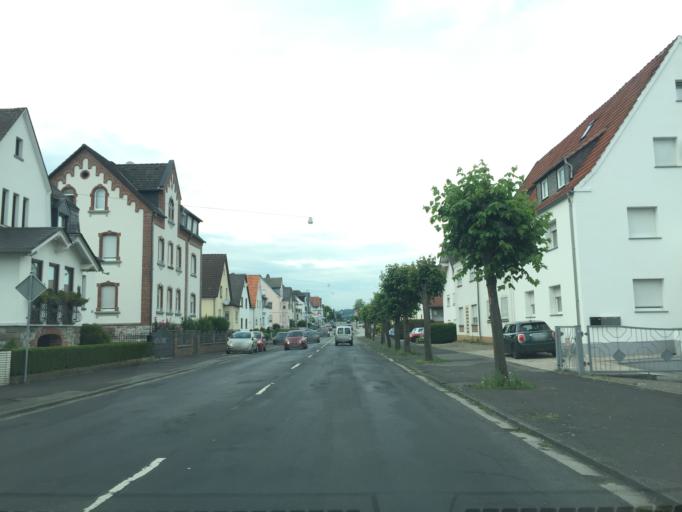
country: DE
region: Hesse
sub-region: Regierungsbezirk Giessen
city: Elz
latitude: 50.4404
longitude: 8.0390
